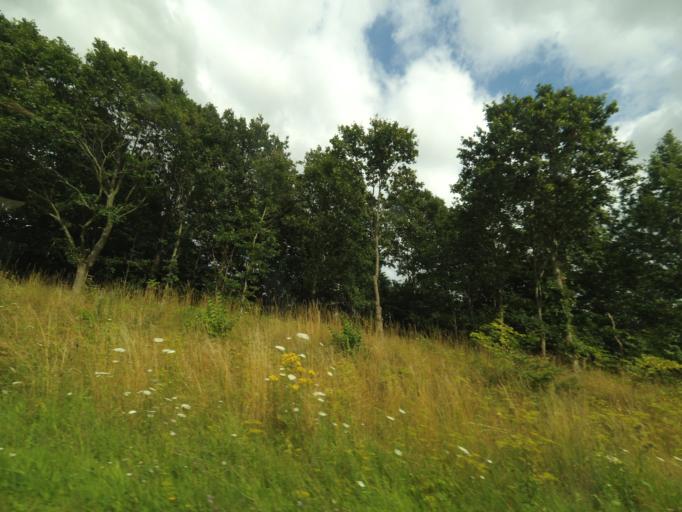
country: DK
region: South Denmark
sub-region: Odense Kommune
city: Stige
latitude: 55.4392
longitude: 10.3759
